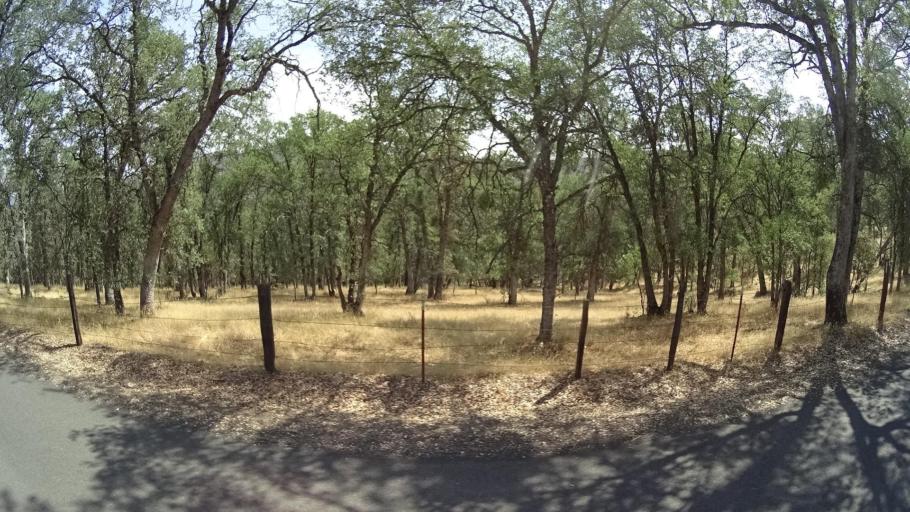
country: US
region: California
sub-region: Tuolumne County
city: Tuolumne City
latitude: 37.7124
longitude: -120.1802
